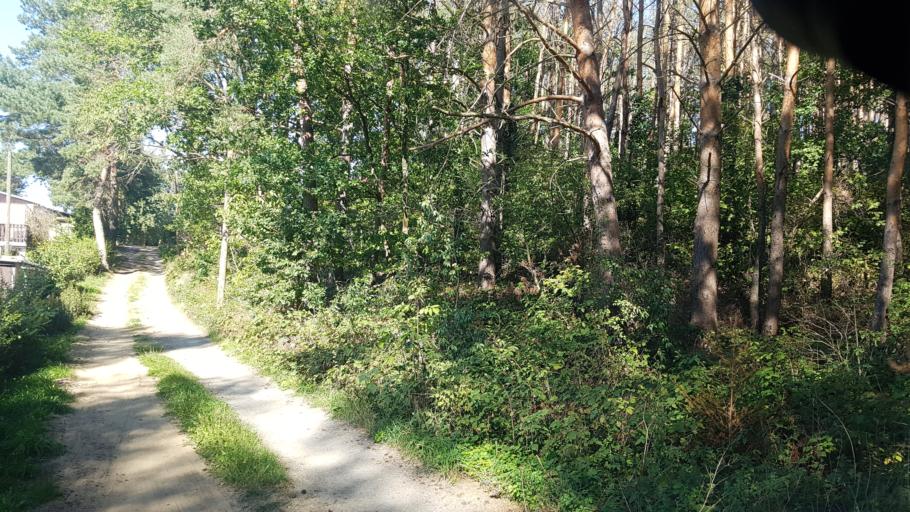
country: DE
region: Brandenburg
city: Hirschfeld
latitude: 51.3805
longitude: 13.6210
